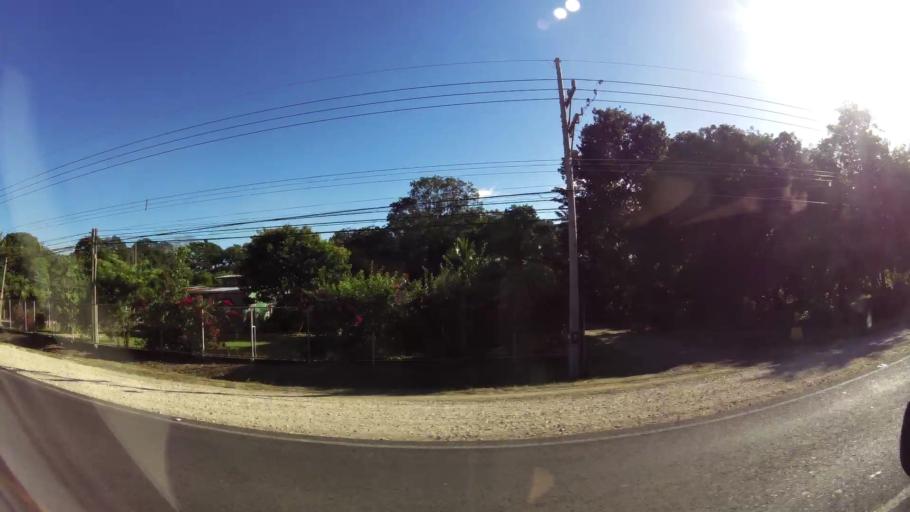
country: CR
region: Guanacaste
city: Belen
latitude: 10.4606
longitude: -85.5582
